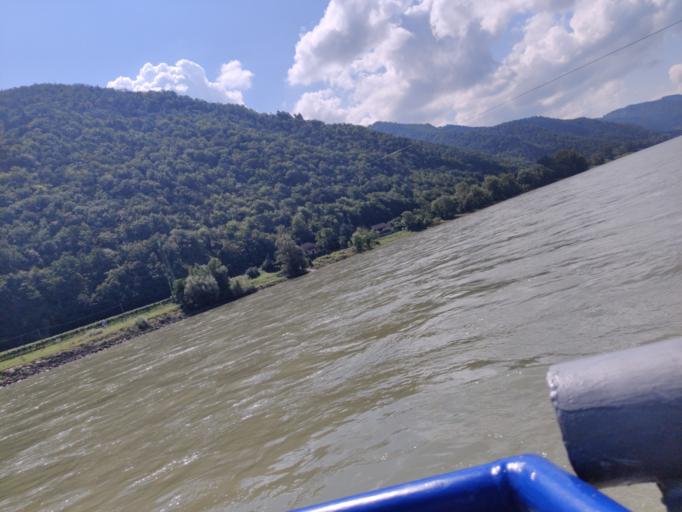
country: AT
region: Lower Austria
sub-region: Politischer Bezirk Krems
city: Durnstein
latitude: 48.3941
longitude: 15.4735
